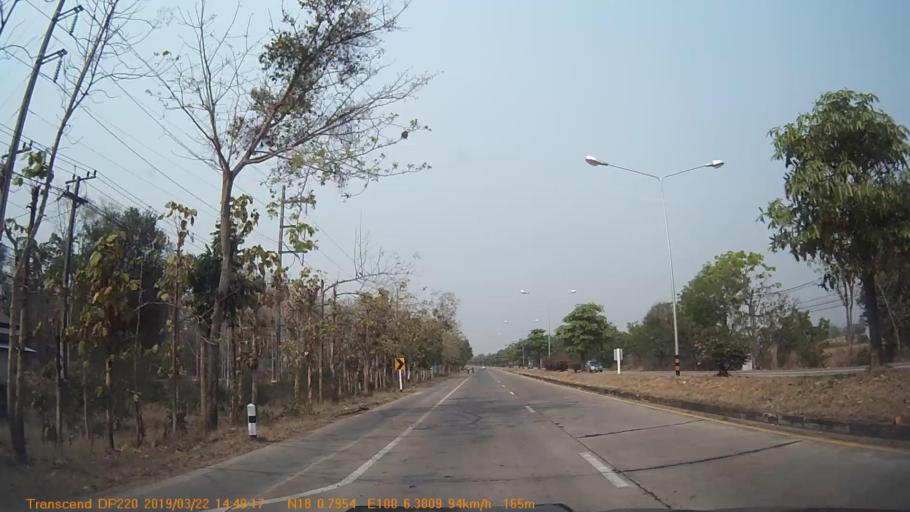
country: TH
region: Phrae
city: Sung Men
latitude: 18.0135
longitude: 100.1065
